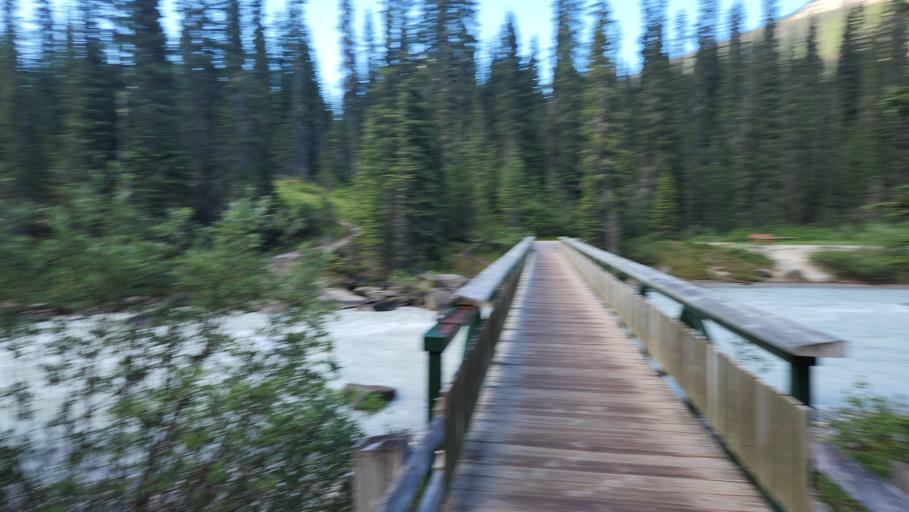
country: CA
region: Alberta
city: Lake Louise
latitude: 51.4963
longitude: -116.4807
